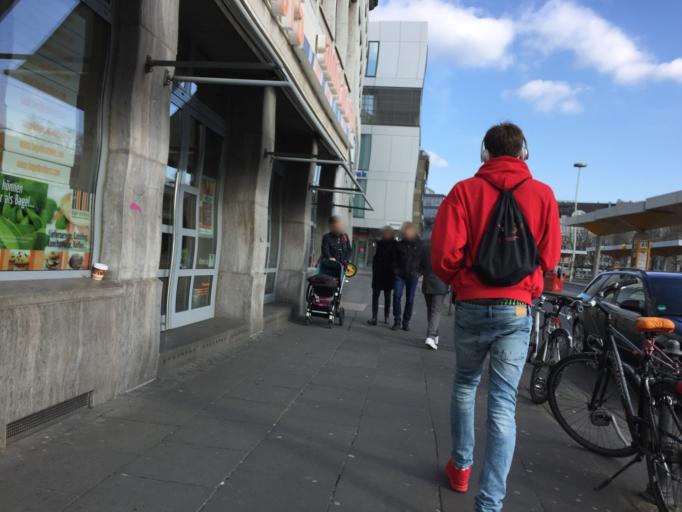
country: DE
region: North Rhine-Westphalia
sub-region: Regierungsbezirk Koln
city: Bonn
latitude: 50.7323
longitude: 7.0986
